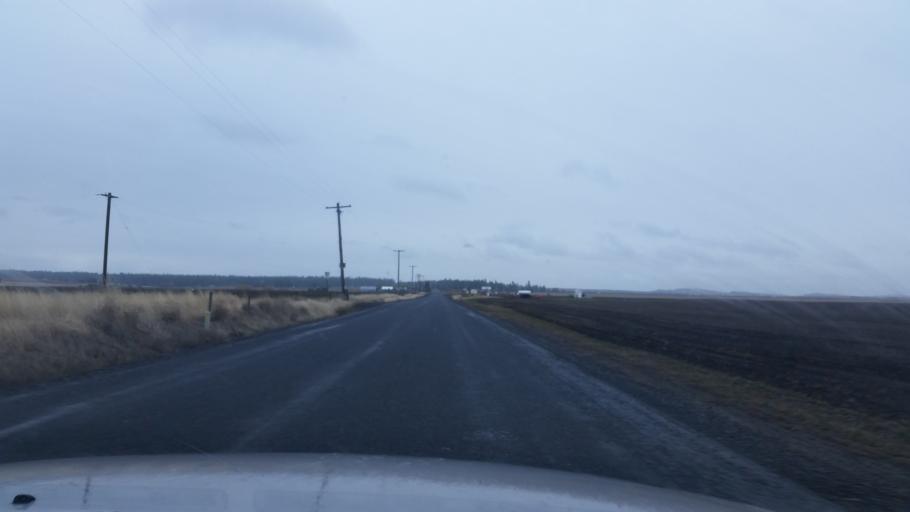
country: US
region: Washington
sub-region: Spokane County
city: Medical Lake
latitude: 47.6144
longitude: -117.7623
